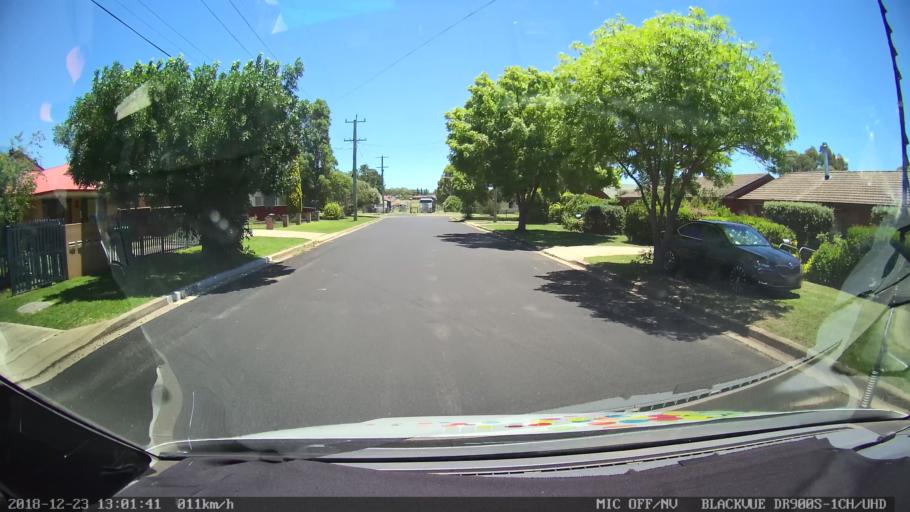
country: AU
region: New South Wales
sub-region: Armidale Dumaresq
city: Armidale
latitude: -30.5070
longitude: 151.6494
